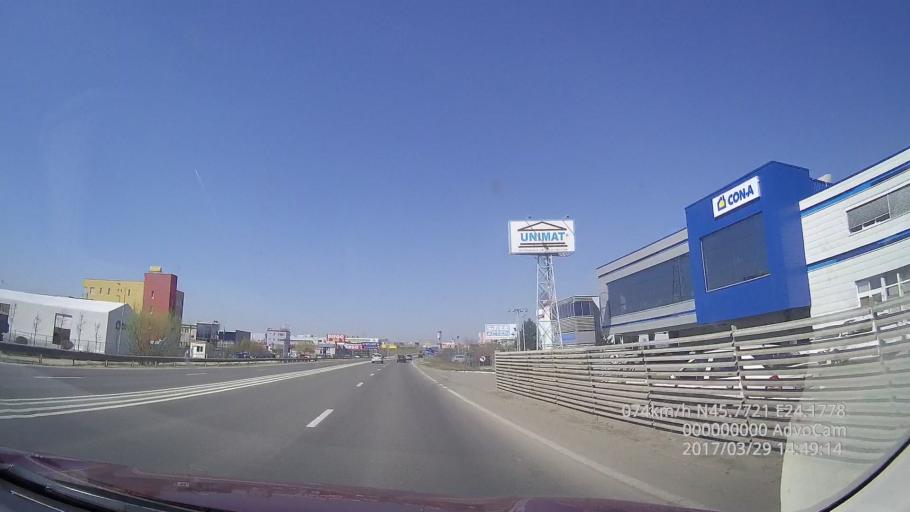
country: RO
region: Sibiu
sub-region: Comuna Selimbar
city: Selimbar
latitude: 45.7724
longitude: 24.1775
